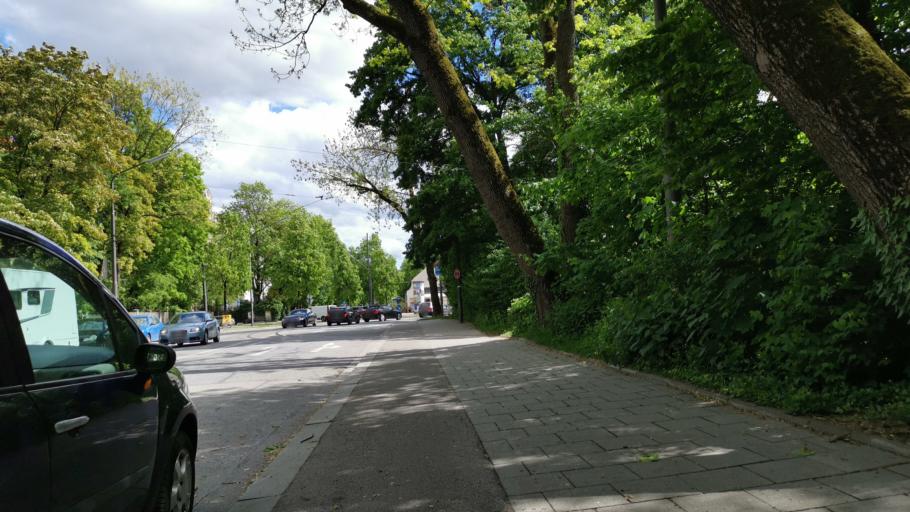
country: DE
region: Bavaria
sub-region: Upper Bavaria
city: Munich
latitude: 48.1574
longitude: 11.5308
